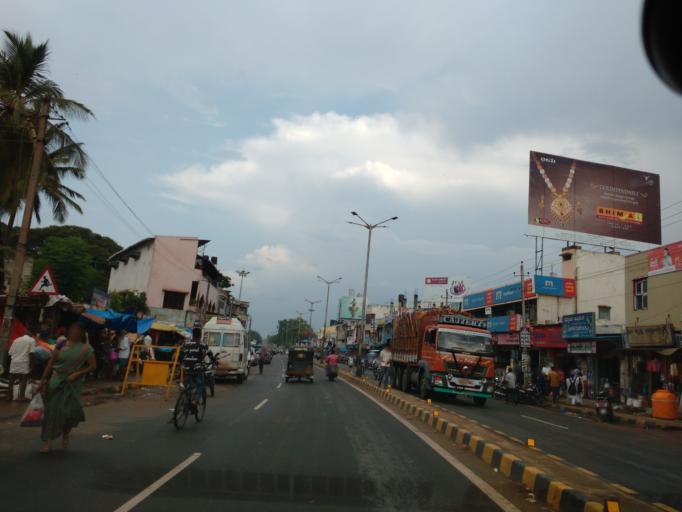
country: IN
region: Karnataka
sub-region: Hassan
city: Arsikere
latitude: 13.3149
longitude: 76.2553
